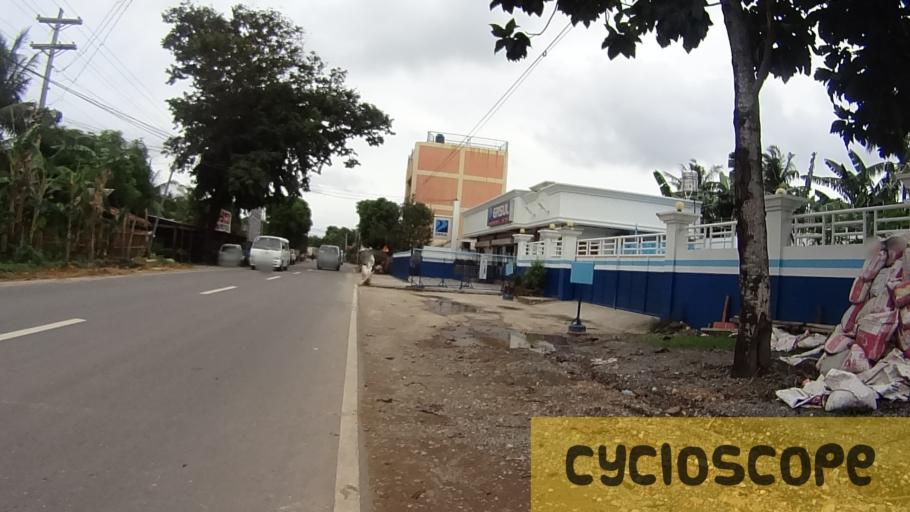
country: PH
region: Western Visayas
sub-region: Province of Aklan
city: Caticlan
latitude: 11.9316
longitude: 121.9610
